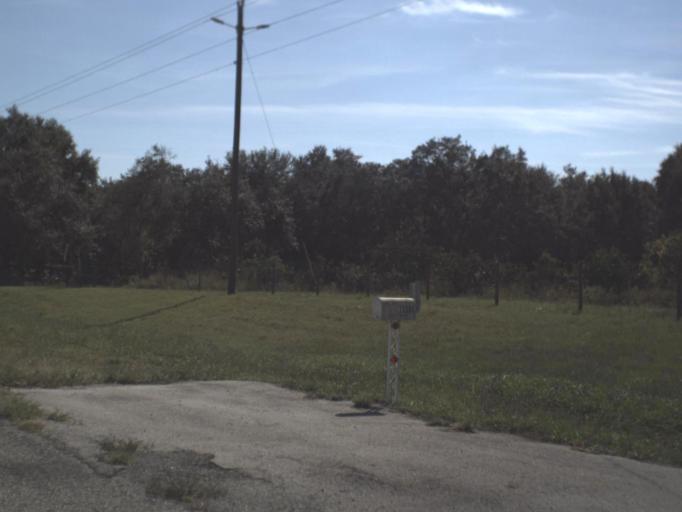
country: US
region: Florida
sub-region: Highlands County
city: Sebring
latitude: 27.3940
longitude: -81.4156
